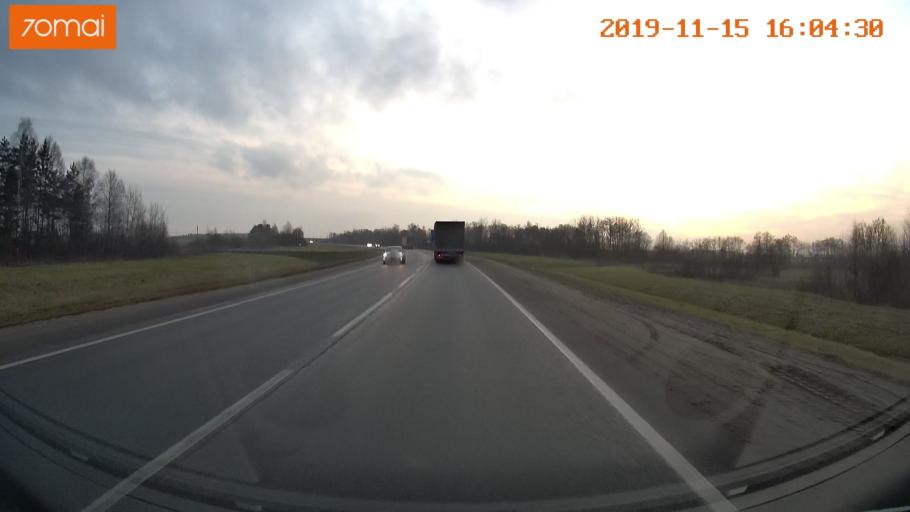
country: RU
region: Jaroslavl
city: Yaroslavl
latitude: 57.7474
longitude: 39.9007
